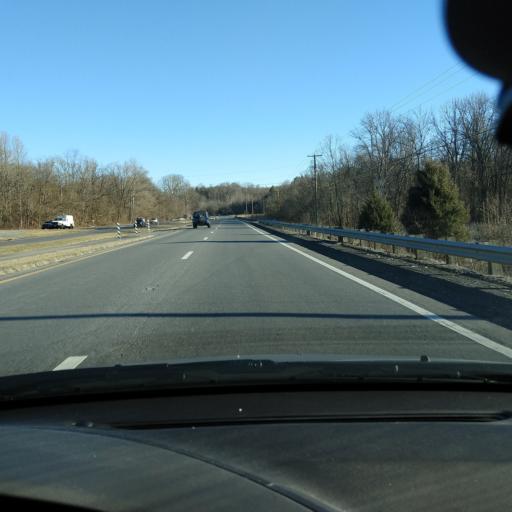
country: US
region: Virginia
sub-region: Botetourt County
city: Blue Ridge
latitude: 37.3724
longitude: -79.7009
